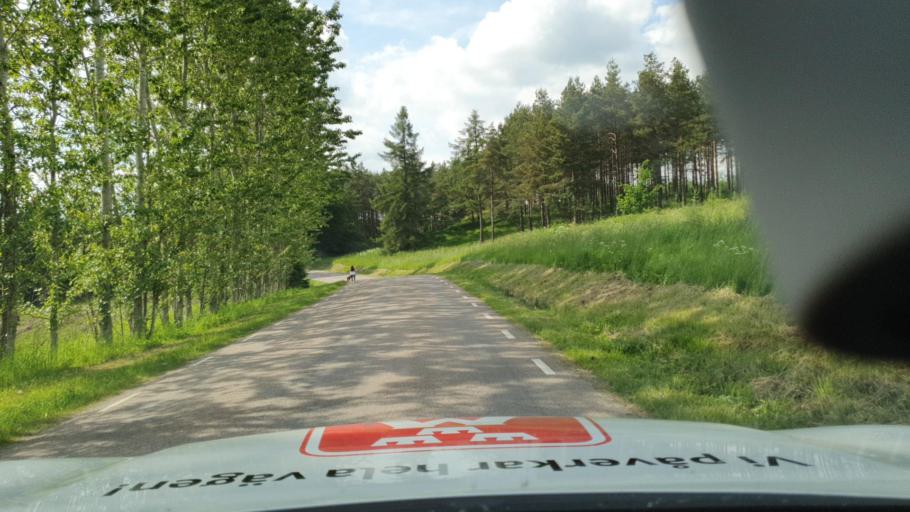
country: SE
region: Skane
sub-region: Skurups Kommun
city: Skurup
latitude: 55.5547
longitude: 13.5033
